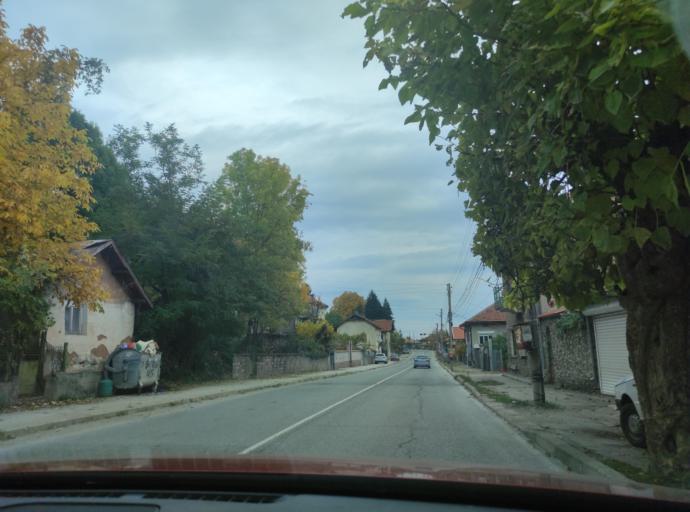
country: BG
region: Montana
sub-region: Obshtina Berkovitsa
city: Berkovitsa
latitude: 43.2020
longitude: 23.1614
